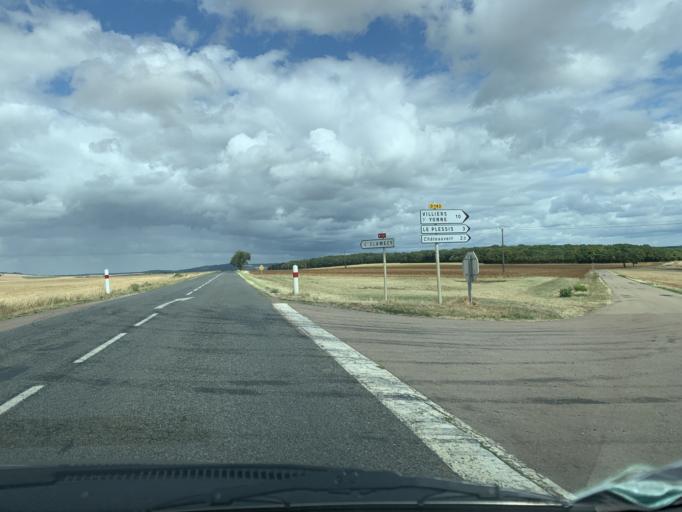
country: FR
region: Bourgogne
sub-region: Departement de la Nievre
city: Clamecy
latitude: 47.4207
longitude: 3.4663
